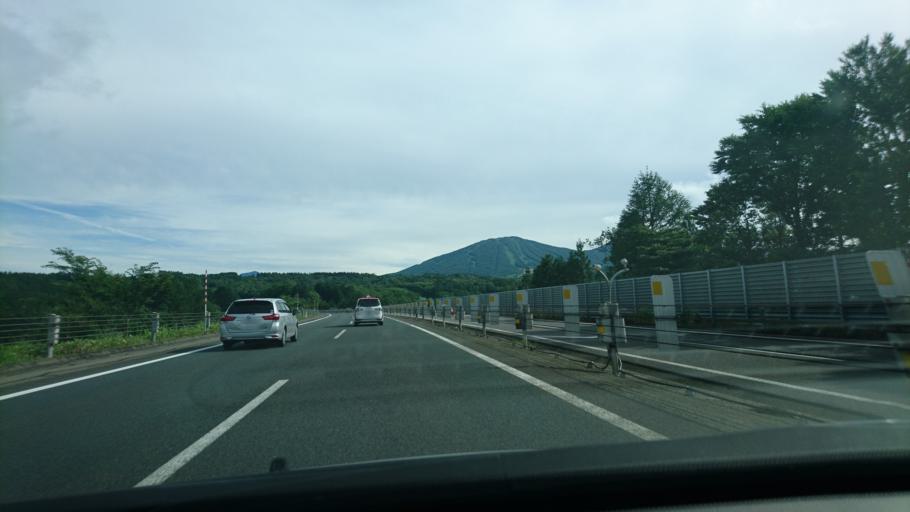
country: JP
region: Akita
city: Hanawa
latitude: 40.0277
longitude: 140.9831
